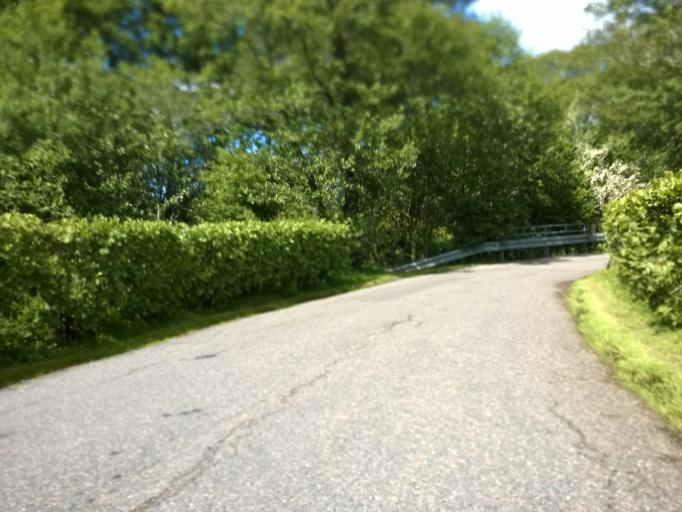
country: DK
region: Central Jutland
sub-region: Holstebro Kommune
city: Vinderup
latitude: 56.4278
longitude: 8.7439
